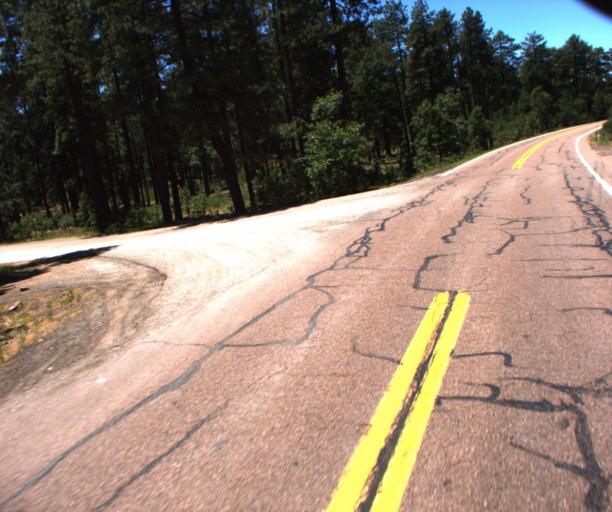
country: US
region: Arizona
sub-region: Gila County
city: Pine
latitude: 34.4555
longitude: -111.3963
